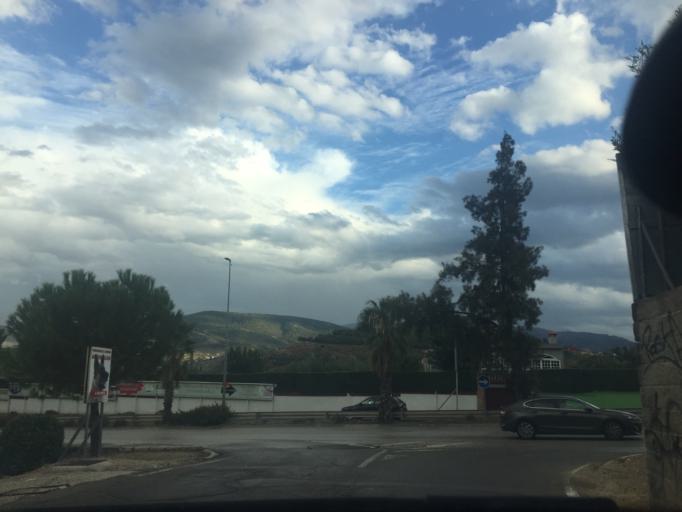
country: ES
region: Andalusia
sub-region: Provincia de Jaen
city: Jaen
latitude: 37.7729
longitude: -3.7711
